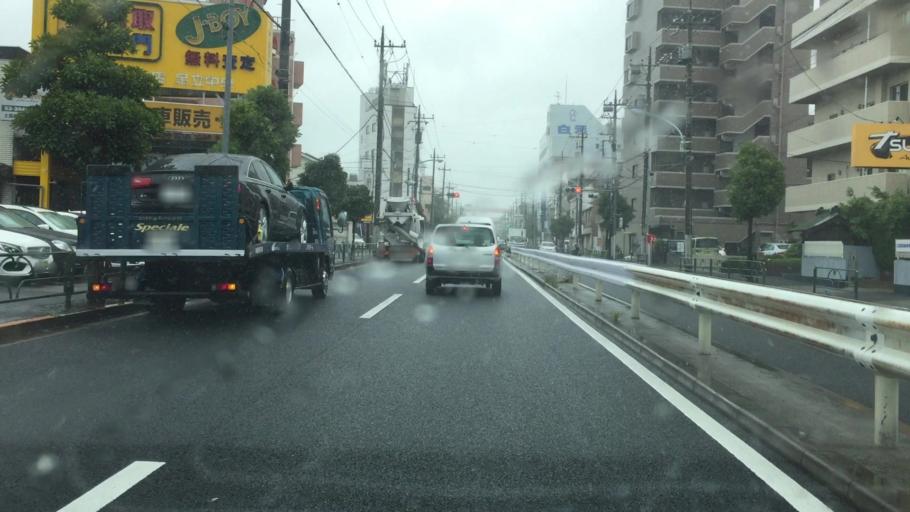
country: JP
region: Saitama
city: Soka
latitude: 35.7678
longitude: 139.7860
